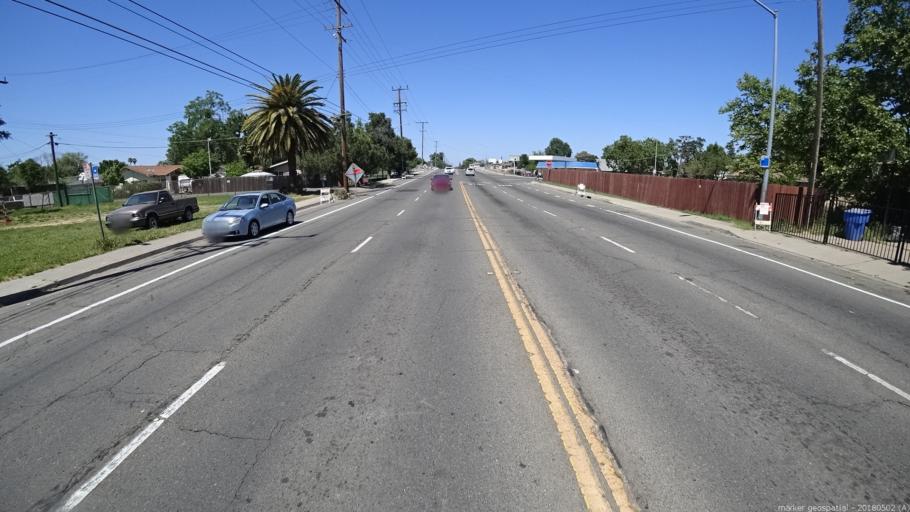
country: US
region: California
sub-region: Sacramento County
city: Sacramento
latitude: 38.6244
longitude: -121.4462
